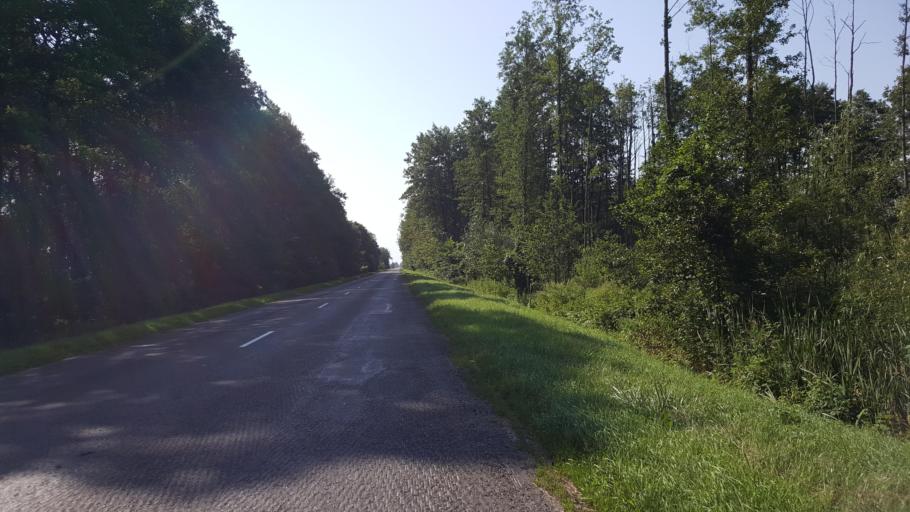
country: BY
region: Brest
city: Zhabinka
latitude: 52.2702
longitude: 23.9558
